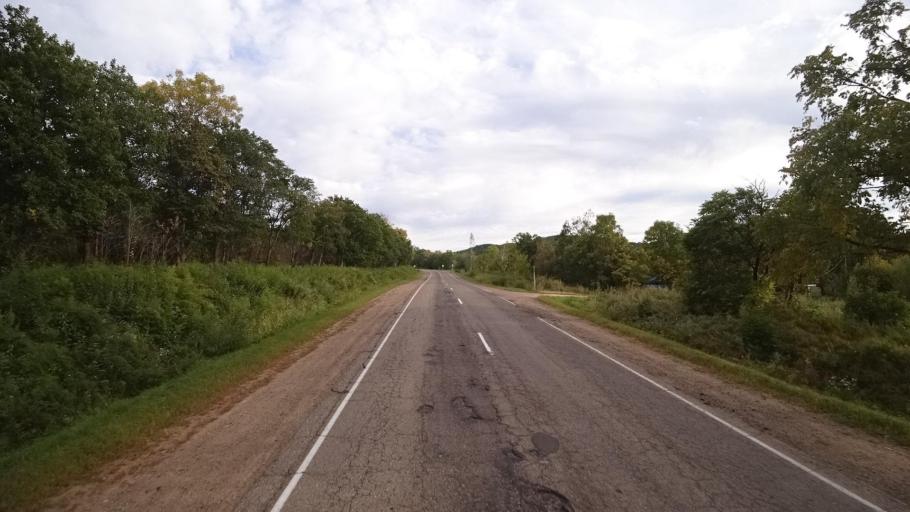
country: RU
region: Primorskiy
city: Yakovlevka
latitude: 44.4139
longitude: 133.4536
